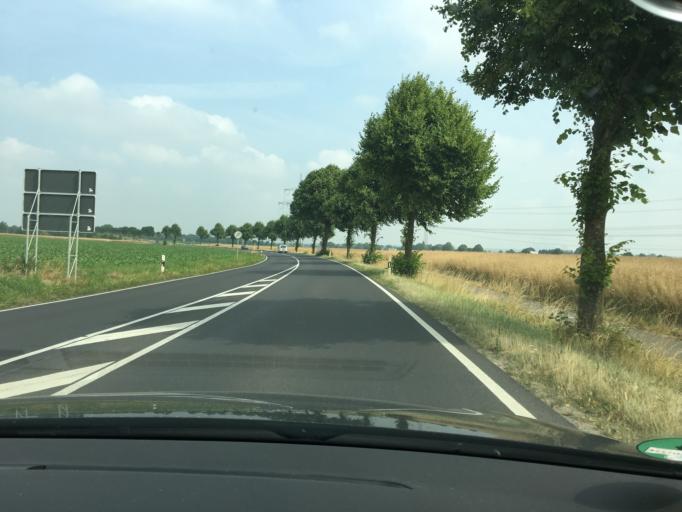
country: DE
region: North Rhine-Westphalia
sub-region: Regierungsbezirk Koln
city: Bergheim
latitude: 50.9136
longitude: 6.6180
